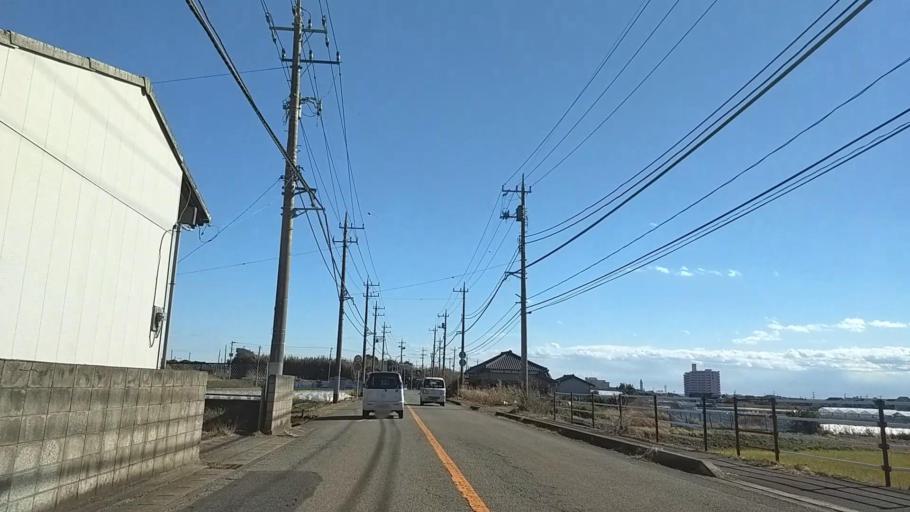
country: JP
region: Chiba
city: Tateyama
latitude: 34.9093
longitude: 139.8746
